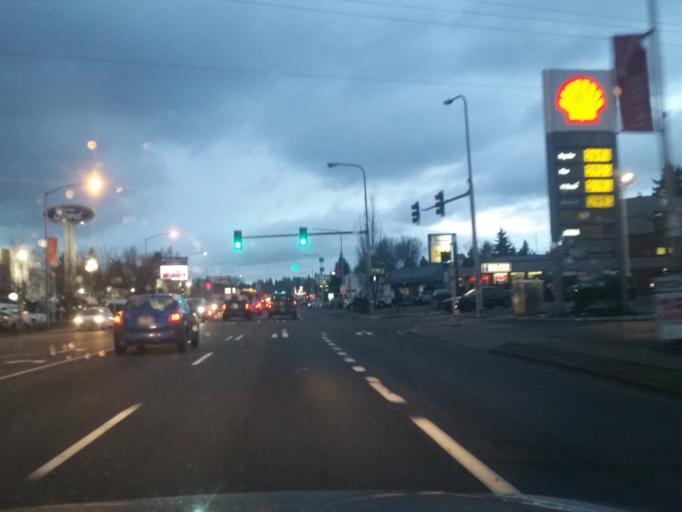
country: US
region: Washington
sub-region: King County
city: Lake Forest Park
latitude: 47.7118
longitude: -122.2997
